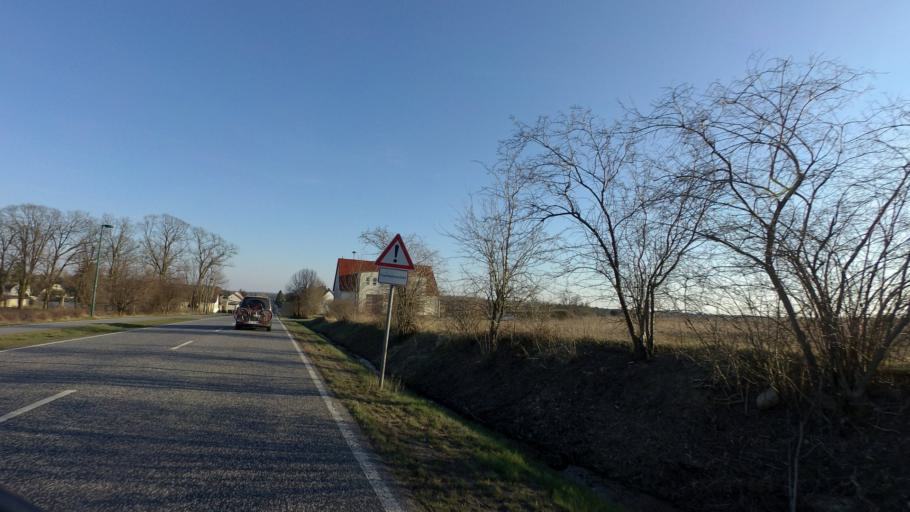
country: DE
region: Brandenburg
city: Britz
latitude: 52.8812
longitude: 13.8160
